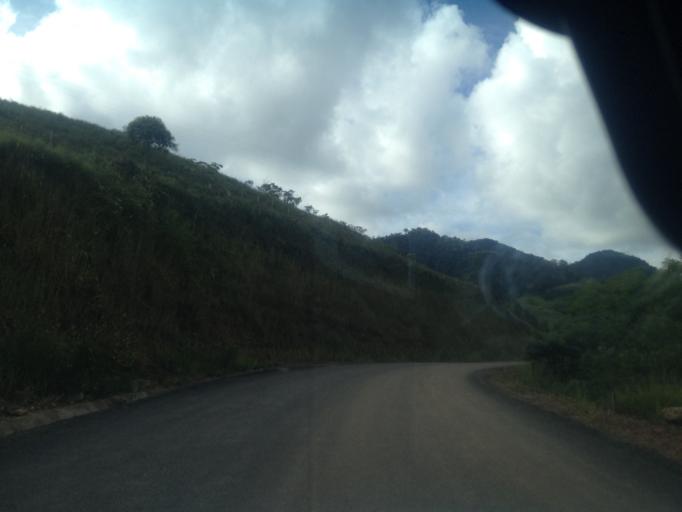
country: BR
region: Rio de Janeiro
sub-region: Quatis
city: Quatis
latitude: -22.2097
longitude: -44.2411
